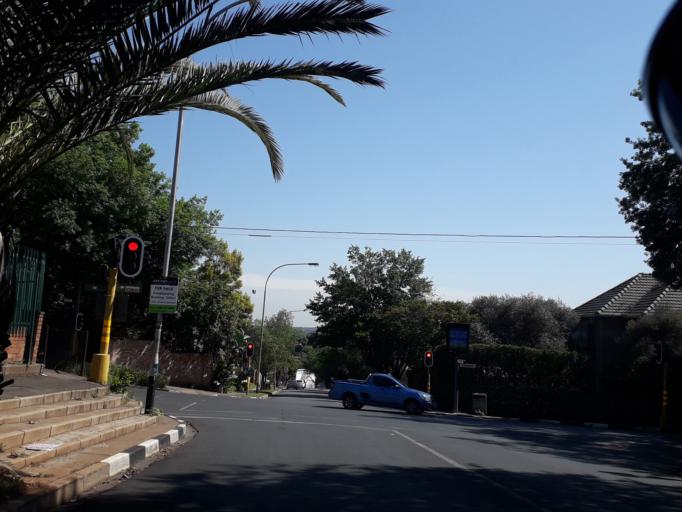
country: ZA
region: Gauteng
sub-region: City of Johannesburg Metropolitan Municipality
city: Johannesburg
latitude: -26.1478
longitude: 28.0158
